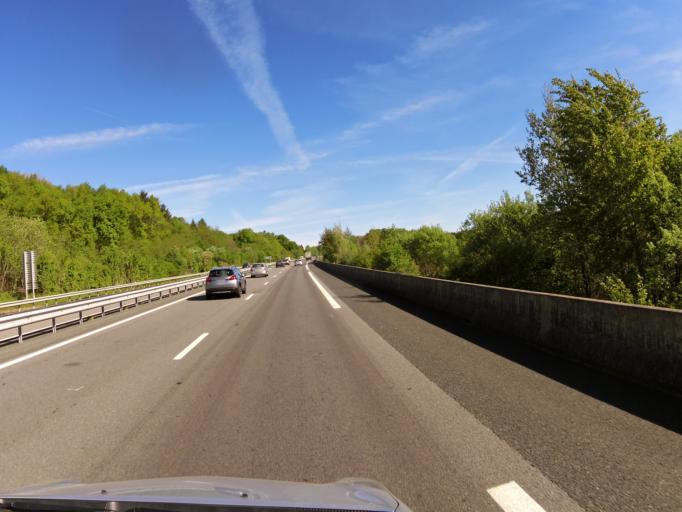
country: FR
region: Limousin
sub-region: Departement de la Correze
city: Vigeois
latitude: 45.3489
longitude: 1.5699
